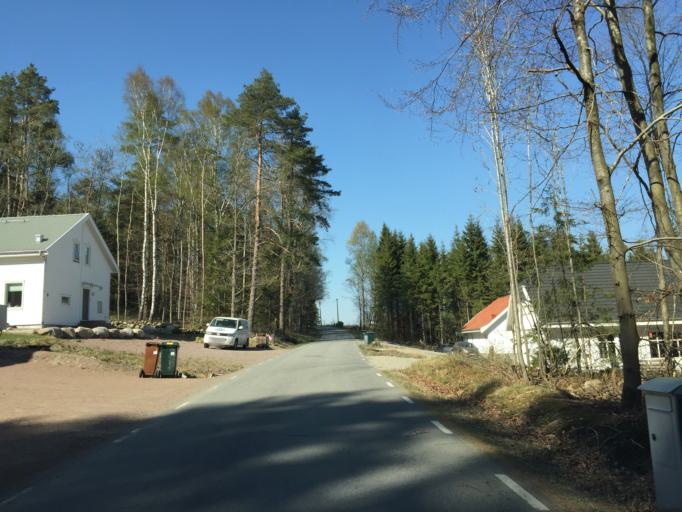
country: SE
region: Vaestra Goetaland
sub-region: Ale Kommun
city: Surte
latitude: 57.8254
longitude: 11.9896
